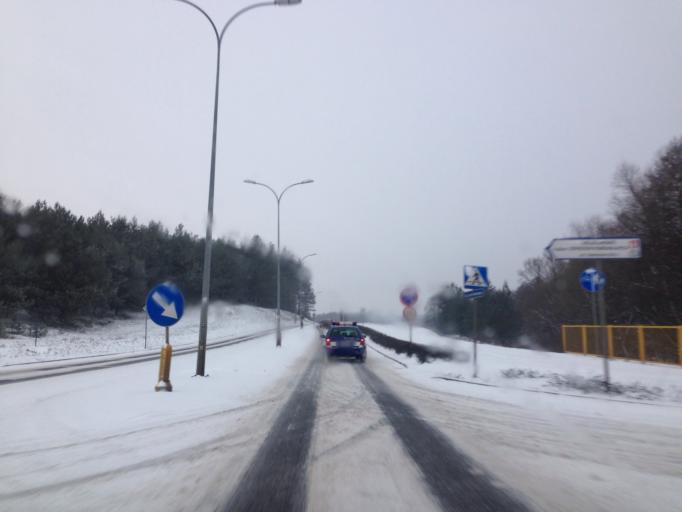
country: PL
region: Kujawsko-Pomorskie
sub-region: Powiat brodnicki
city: Brodnica
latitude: 53.2380
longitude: 19.3845
